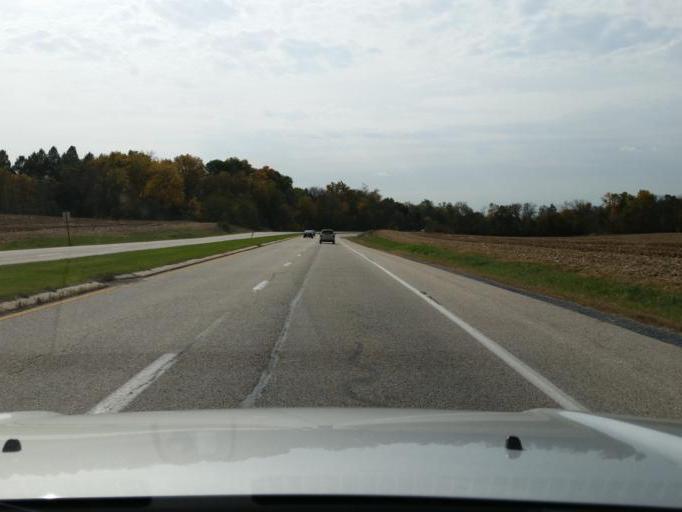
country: US
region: Pennsylvania
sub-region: Dauphin County
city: Palmdale
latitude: 40.3074
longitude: -76.6198
